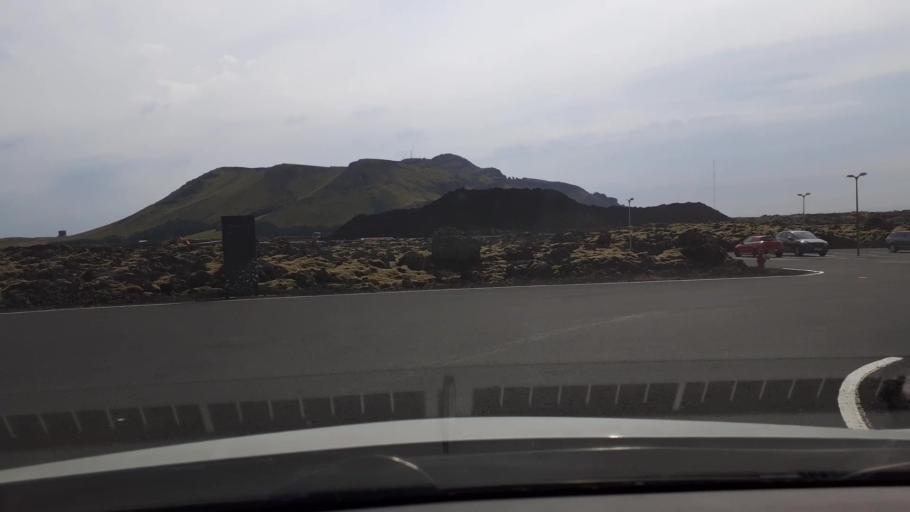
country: IS
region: Southern Peninsula
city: Grindavik
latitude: 63.8809
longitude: -22.4401
